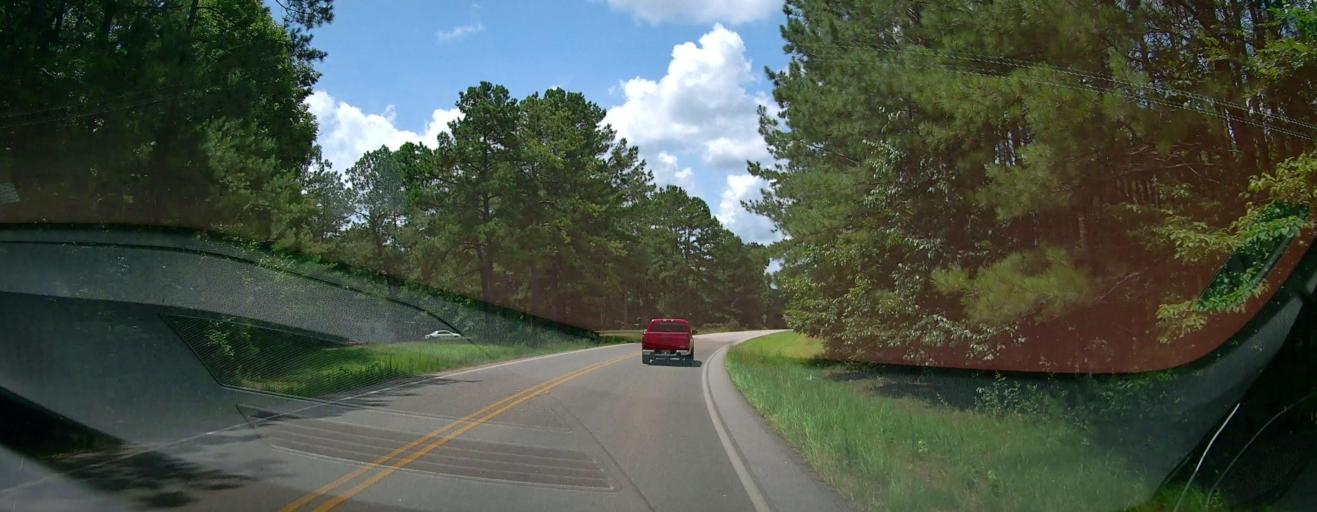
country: US
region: Georgia
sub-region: Meriwether County
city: Greenville
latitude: 33.0876
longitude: -84.7864
